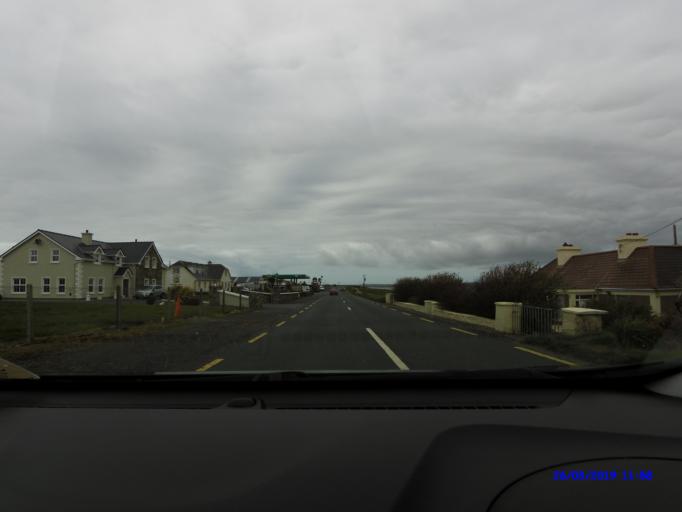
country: IE
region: Connaught
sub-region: Maigh Eo
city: Belmullet
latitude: 54.2076
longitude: -9.9330
